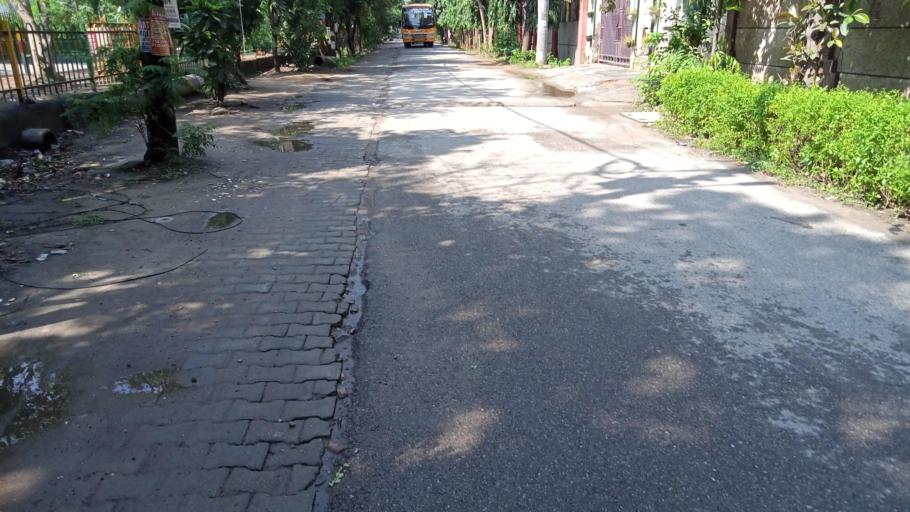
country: IN
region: Uttar Pradesh
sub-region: Ghaziabad
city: Ghaziabad
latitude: 28.6641
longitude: 77.3727
